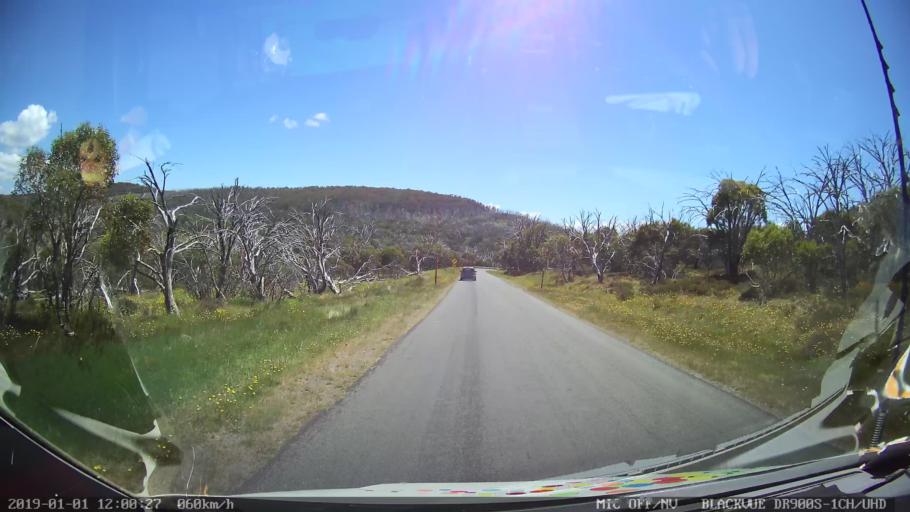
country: AU
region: New South Wales
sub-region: Snowy River
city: Jindabyne
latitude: -35.8847
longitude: 148.4594
